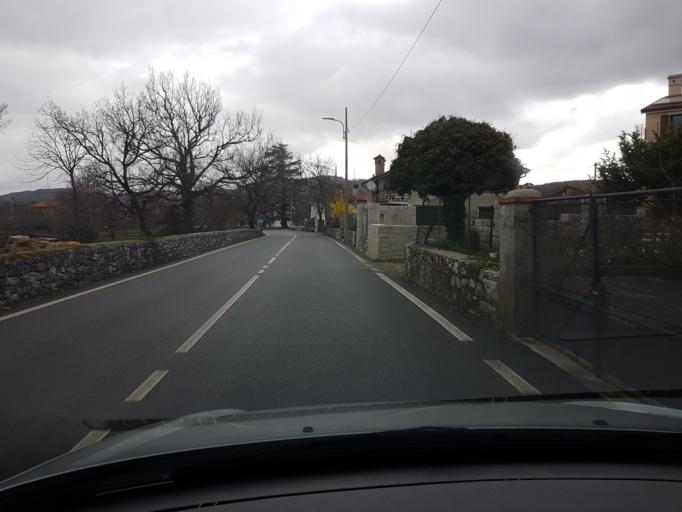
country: IT
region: Friuli Venezia Giulia
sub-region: Provincia di Trieste
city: Sgonico
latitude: 45.7457
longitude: 13.7223
